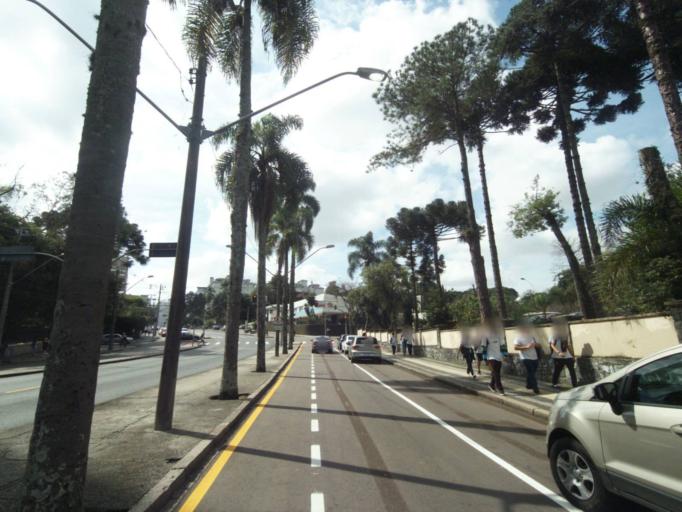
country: BR
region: Parana
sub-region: Curitiba
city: Curitiba
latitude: -25.4230
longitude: -49.2671
